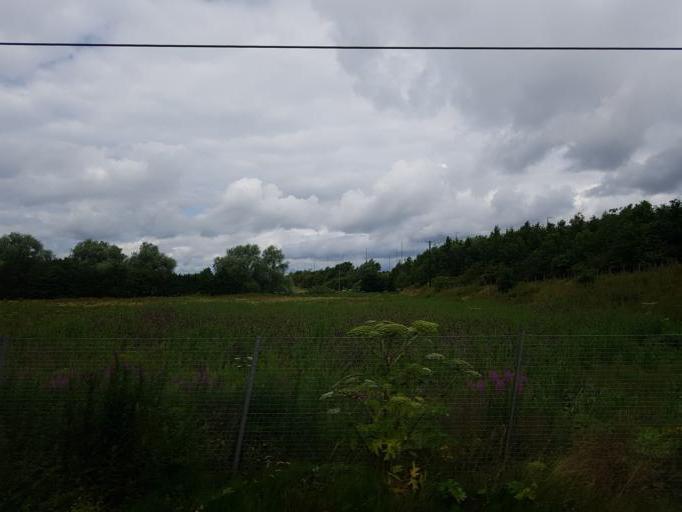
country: GB
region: Scotland
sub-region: Edinburgh
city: Currie
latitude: 55.9266
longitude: -3.3171
